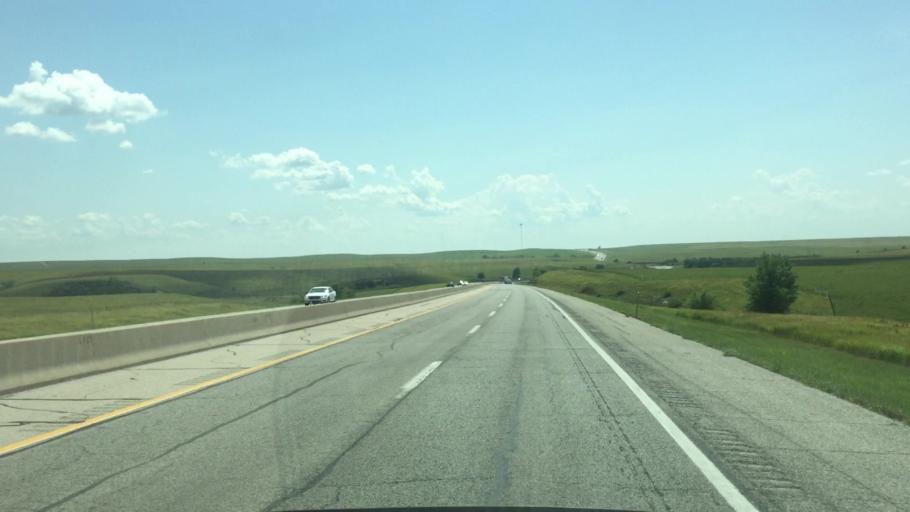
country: US
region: Kansas
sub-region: Chase County
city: Cottonwood Falls
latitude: 38.1830
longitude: -96.4599
